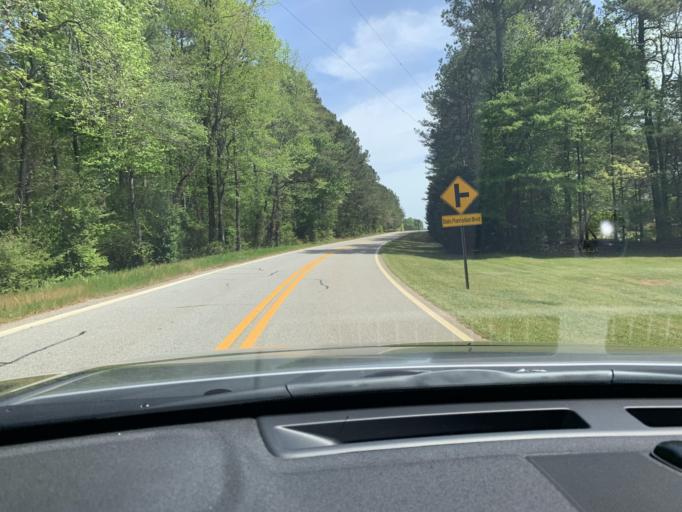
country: US
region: Georgia
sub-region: Oconee County
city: Bogart
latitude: 33.9403
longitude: -83.5669
